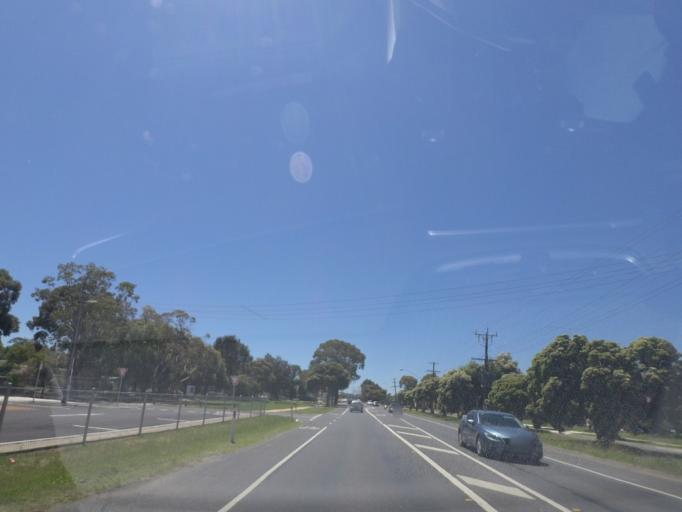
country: AU
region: Victoria
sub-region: Whittlesea
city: Epping
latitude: -37.6417
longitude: 145.0265
